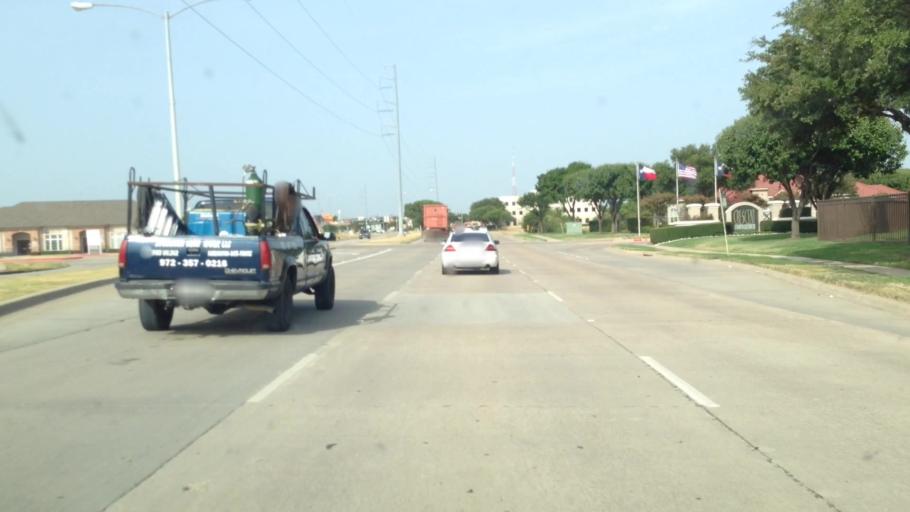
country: US
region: Texas
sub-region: Denton County
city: Lewisville
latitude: 33.0129
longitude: -96.9633
